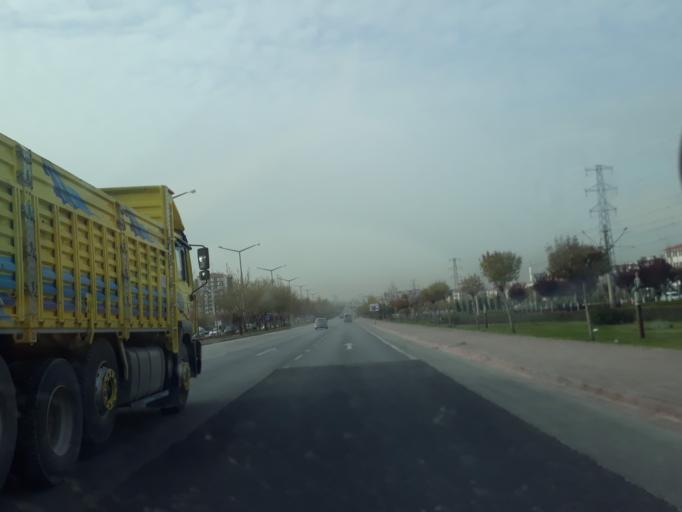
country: TR
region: Konya
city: Asagipinarbasi
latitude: 37.9851
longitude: 32.5175
